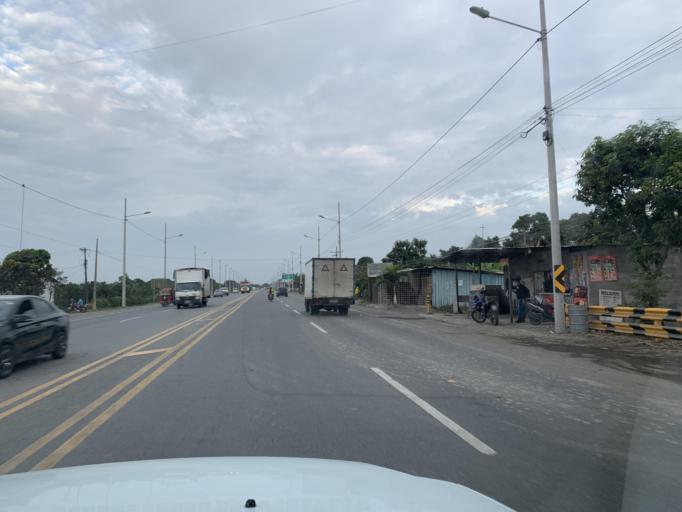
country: EC
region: Guayas
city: Yaguachi Nuevo
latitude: -2.2527
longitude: -79.6325
